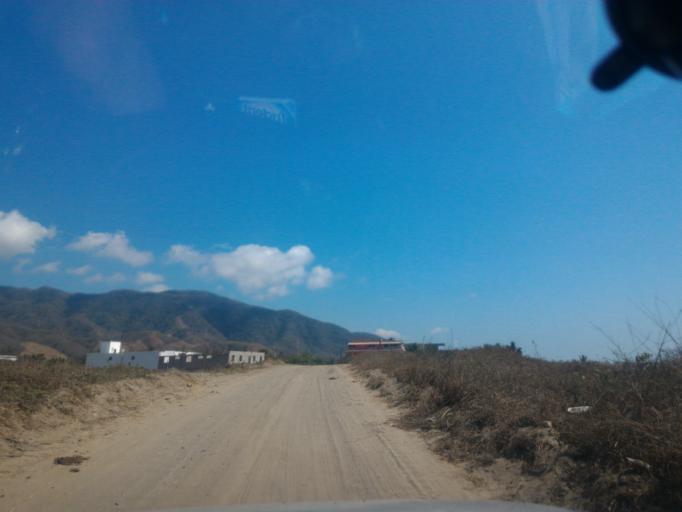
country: MX
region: Michoacan
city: Coahuayana Viejo
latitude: 18.5895
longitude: -103.6846
